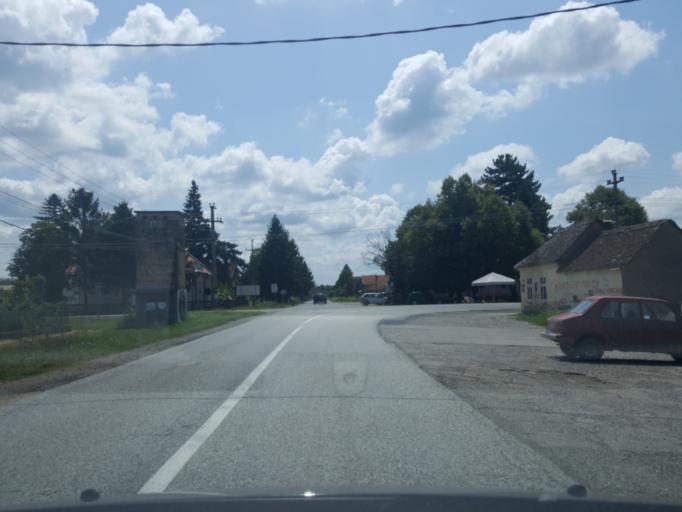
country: RS
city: Metkovic
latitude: 44.8558
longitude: 19.5461
